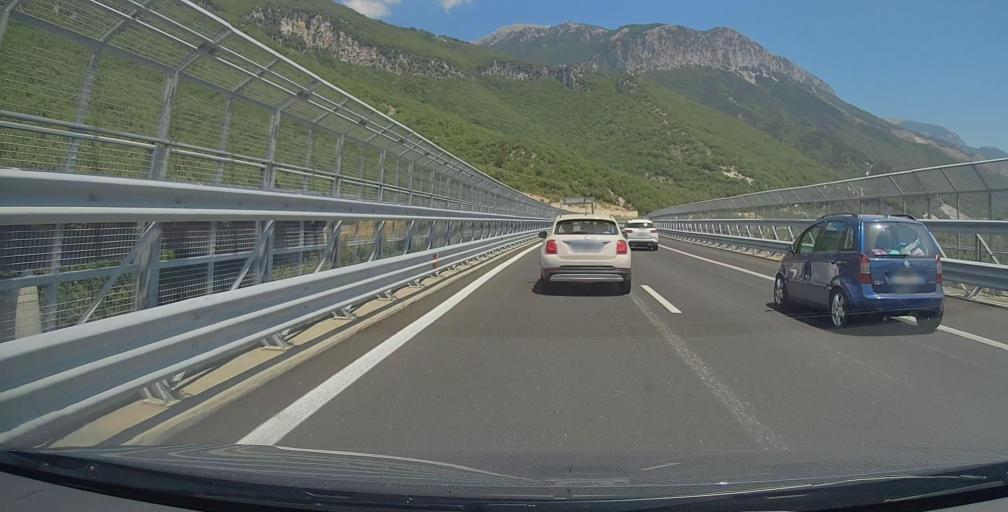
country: IT
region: Calabria
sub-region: Provincia di Cosenza
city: Morano Calabro
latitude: 39.8888
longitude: 16.1416
